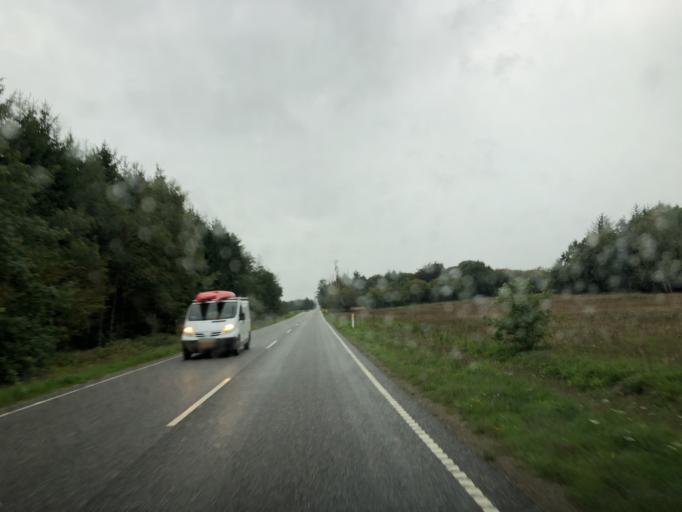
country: DK
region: South Denmark
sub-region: Vejle Kommune
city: Give
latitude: 55.9837
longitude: 9.2709
